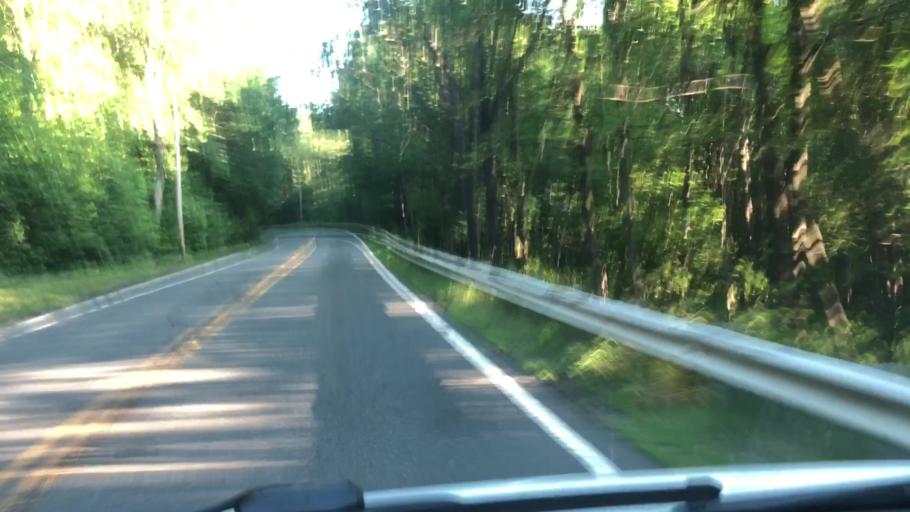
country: US
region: Massachusetts
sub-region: Hampshire County
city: Chesterfield
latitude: 42.4304
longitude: -72.7888
